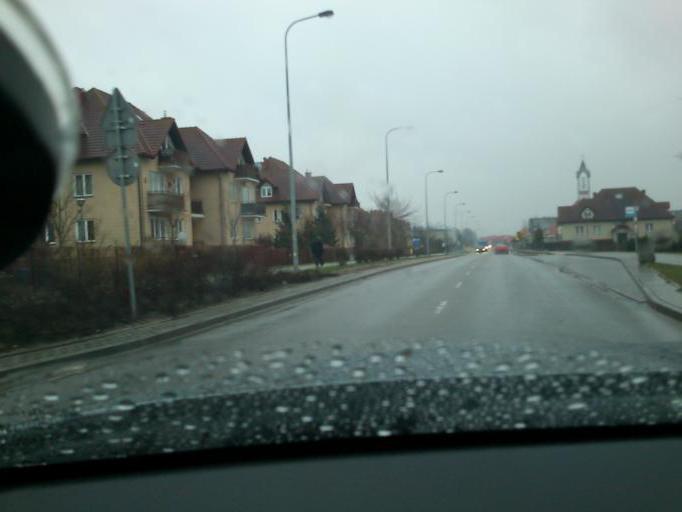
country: PL
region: Pomeranian Voivodeship
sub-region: Gdynia
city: Wielki Kack
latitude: 54.4241
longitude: 18.4790
